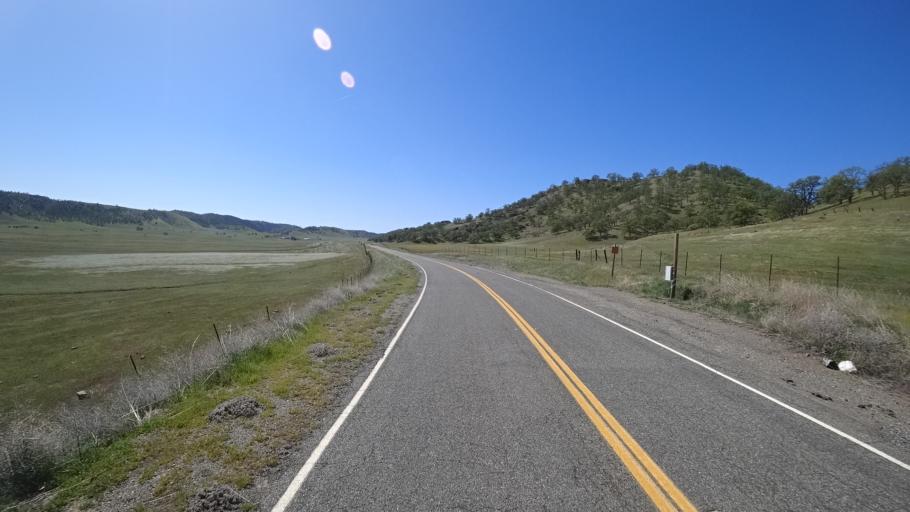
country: US
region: California
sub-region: Tehama County
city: Rancho Tehama Reserve
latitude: 39.7652
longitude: -122.5235
